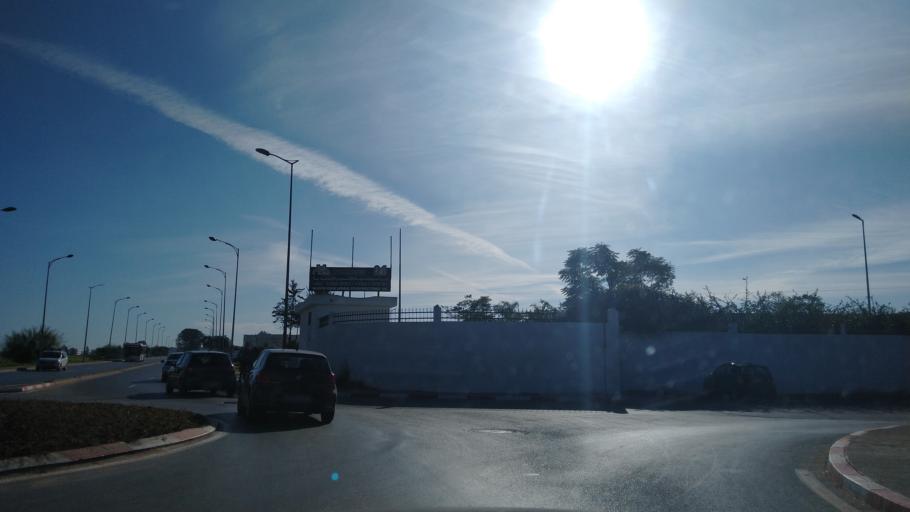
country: MA
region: Rabat-Sale-Zemmour-Zaer
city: Sale
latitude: 34.0208
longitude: -6.7348
